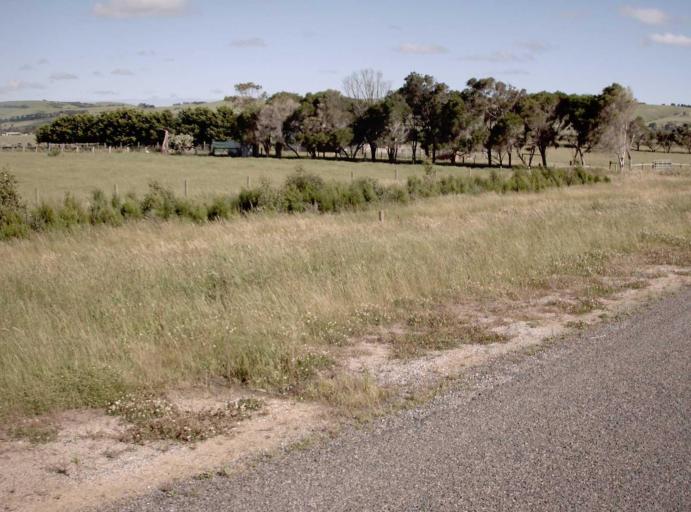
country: AU
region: Victoria
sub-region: Bass Coast
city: North Wonthaggi
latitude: -38.4908
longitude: 145.4637
